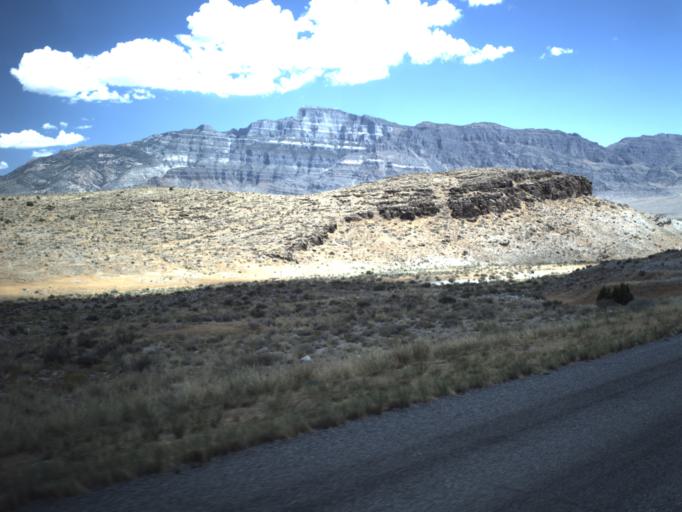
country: US
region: Utah
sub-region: Beaver County
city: Milford
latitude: 39.0858
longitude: -113.5250
